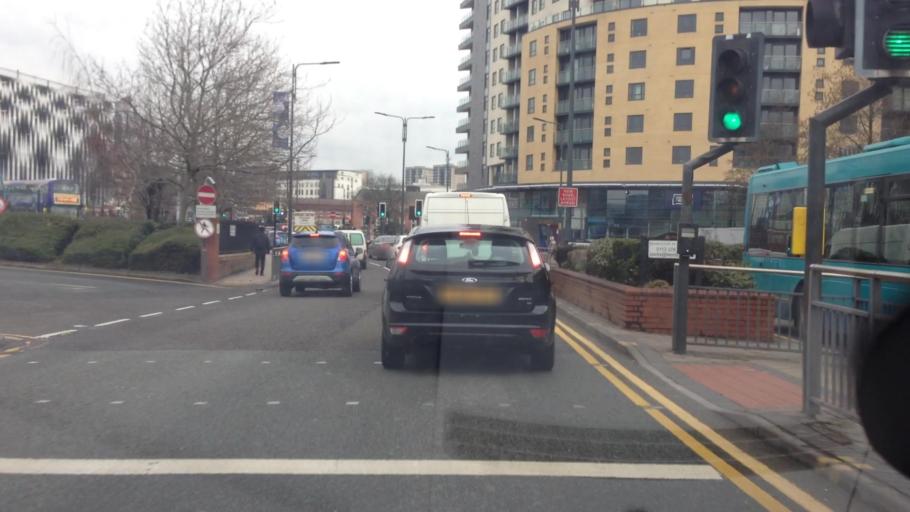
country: GB
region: England
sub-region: City and Borough of Leeds
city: Leeds
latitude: 53.7966
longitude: -1.5344
